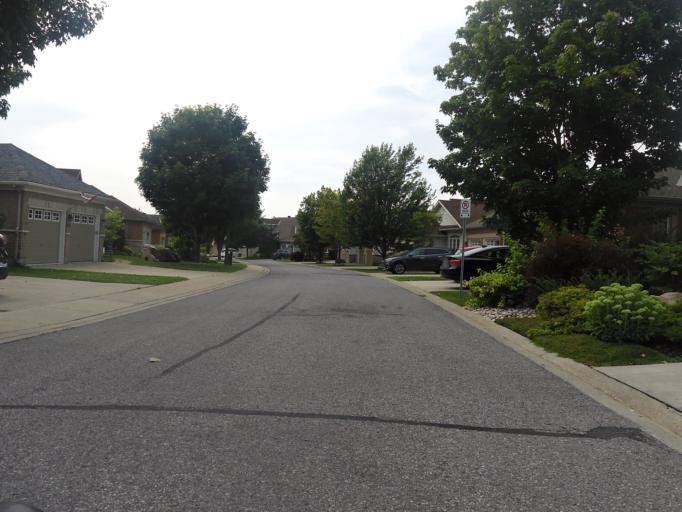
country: CA
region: Ontario
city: Bells Corners
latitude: 45.3160
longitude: -75.9239
